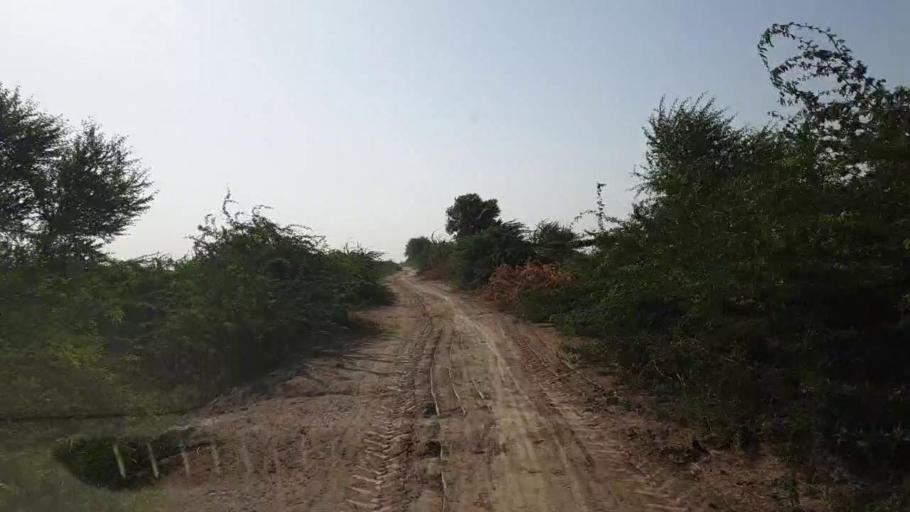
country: PK
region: Sindh
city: Kadhan
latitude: 24.5867
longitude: 69.0779
